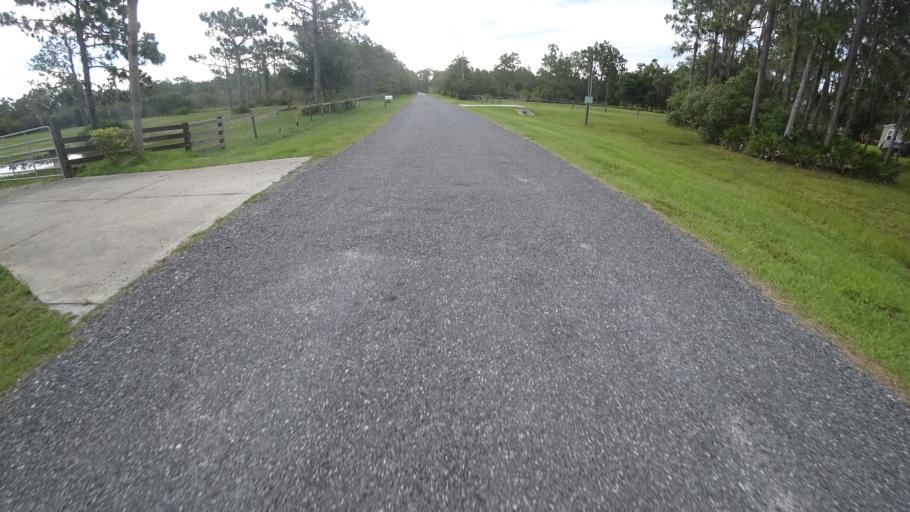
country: US
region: Florida
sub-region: Sarasota County
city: Lake Sarasota
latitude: 27.3977
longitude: -82.2812
